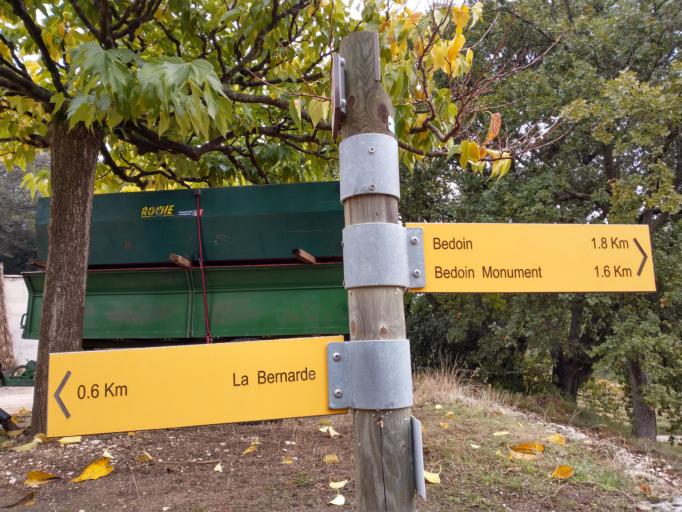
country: FR
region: Provence-Alpes-Cote d'Azur
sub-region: Departement du Vaucluse
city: Bedoin
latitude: 44.1326
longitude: 5.1630
